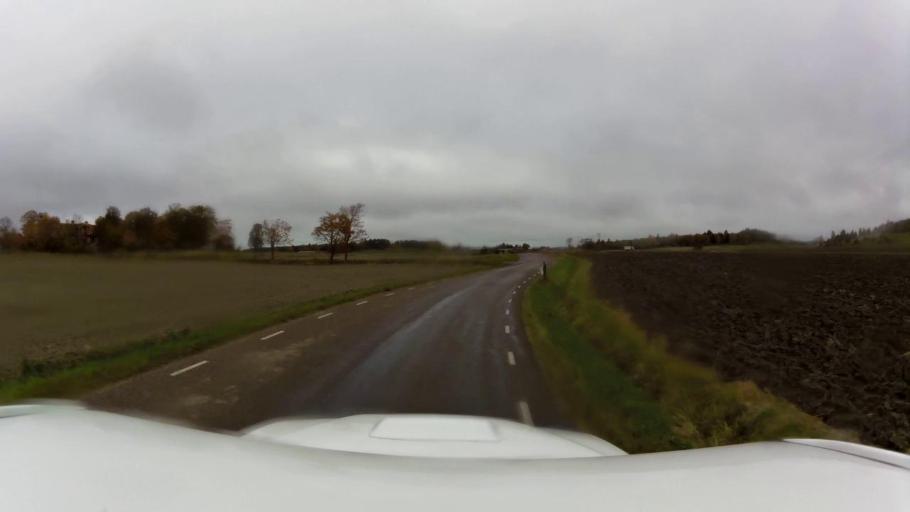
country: SE
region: OEstergoetland
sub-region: Linkopings Kommun
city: Linghem
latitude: 58.4687
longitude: 15.8231
